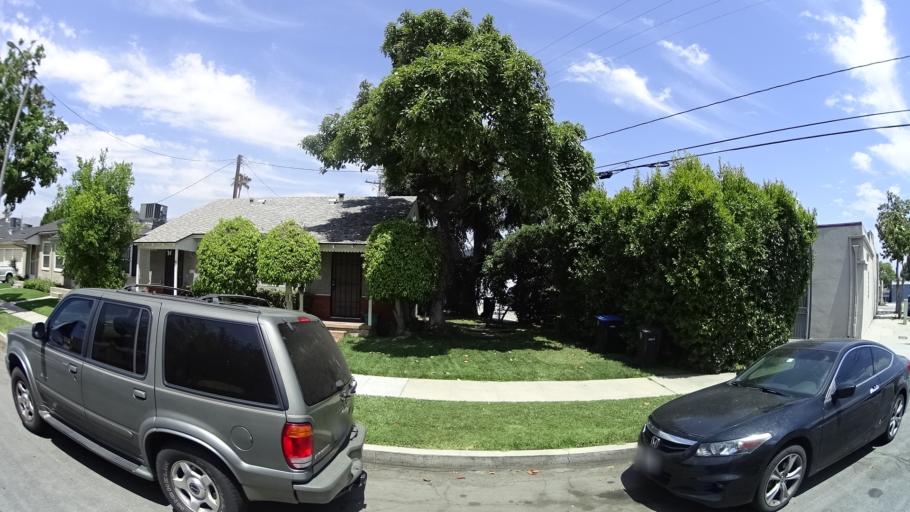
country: US
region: California
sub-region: Los Angeles County
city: Burbank
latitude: 34.1730
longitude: -118.3179
